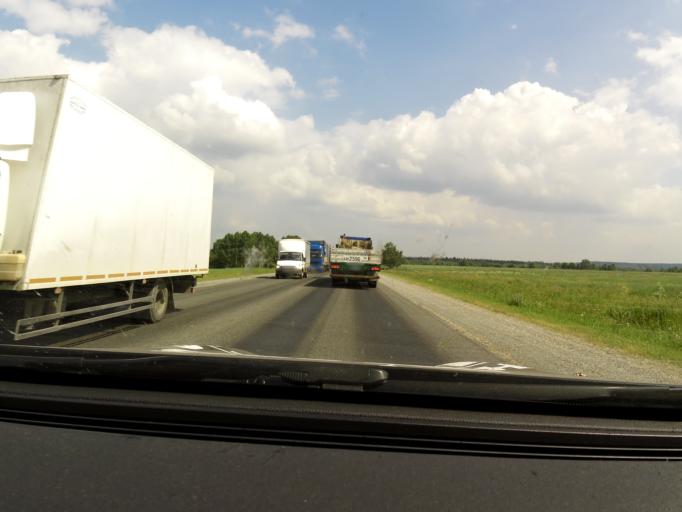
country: RU
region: Sverdlovsk
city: Ufimskiy
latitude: 56.7725
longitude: 58.0718
